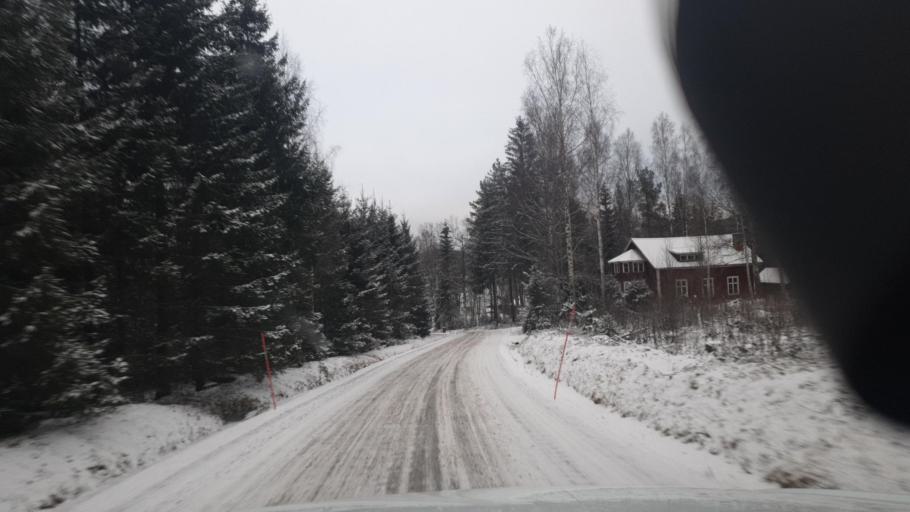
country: SE
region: Vaermland
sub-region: Karlstads Kommun
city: Edsvalla
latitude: 59.6046
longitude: 13.0663
